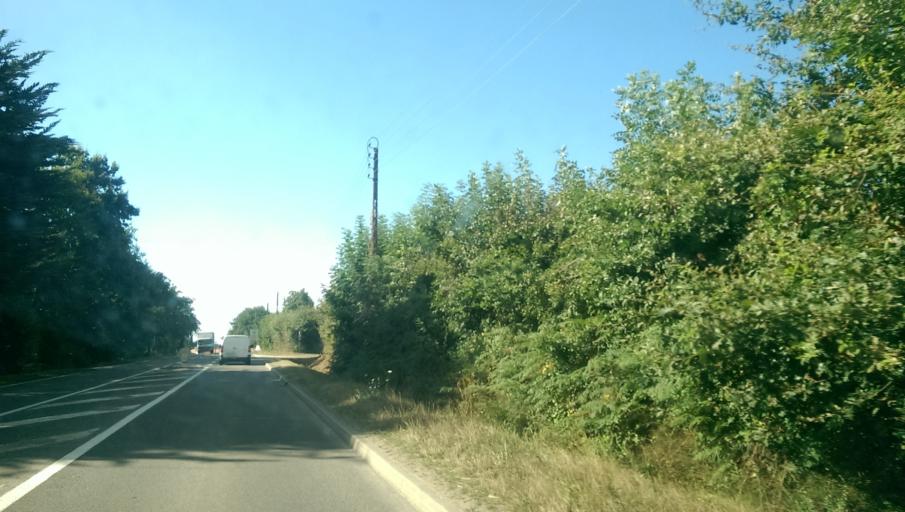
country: FR
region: Pays de la Loire
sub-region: Departement de la Vendee
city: Aizenay
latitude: 46.7282
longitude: -1.6087
